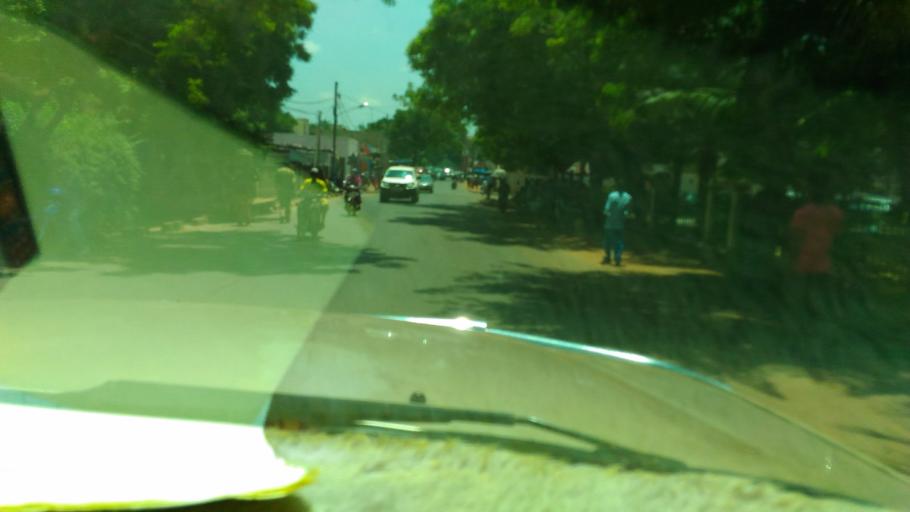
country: ML
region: Bamako
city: Bamako
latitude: 12.6472
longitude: -8.0046
